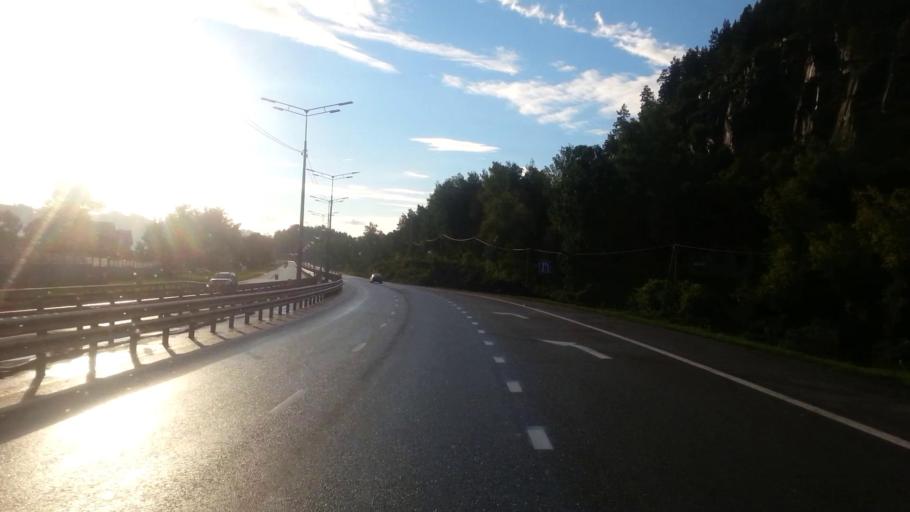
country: RU
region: Altay
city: Souzga
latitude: 51.9191
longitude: 85.8576
